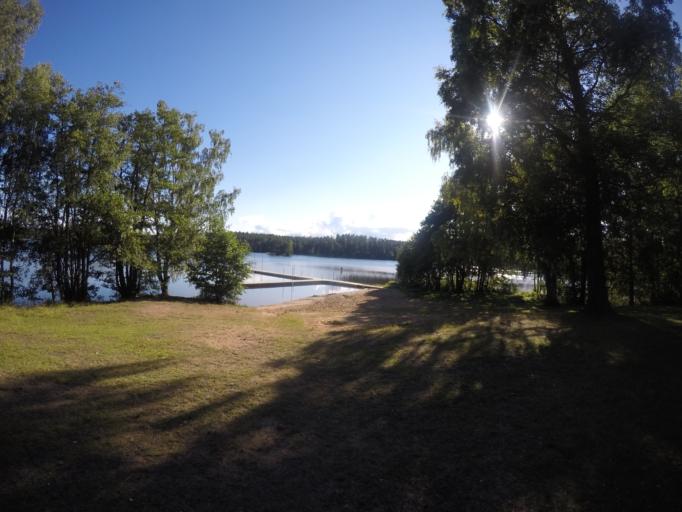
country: SE
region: Joenkoeping
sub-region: Jonkopings Kommun
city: Odensjo
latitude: 57.6689
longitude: 14.1881
